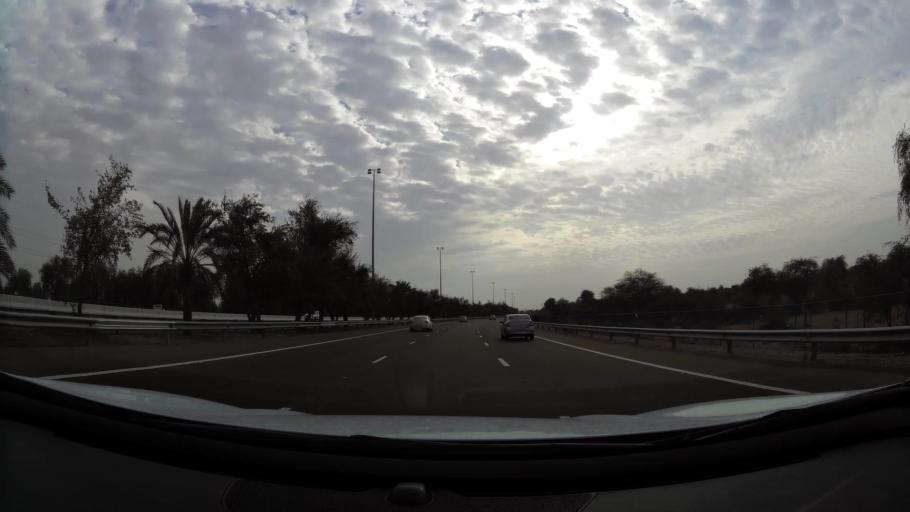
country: AE
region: Abu Dhabi
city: Al Ain
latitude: 24.1689
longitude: 55.2656
